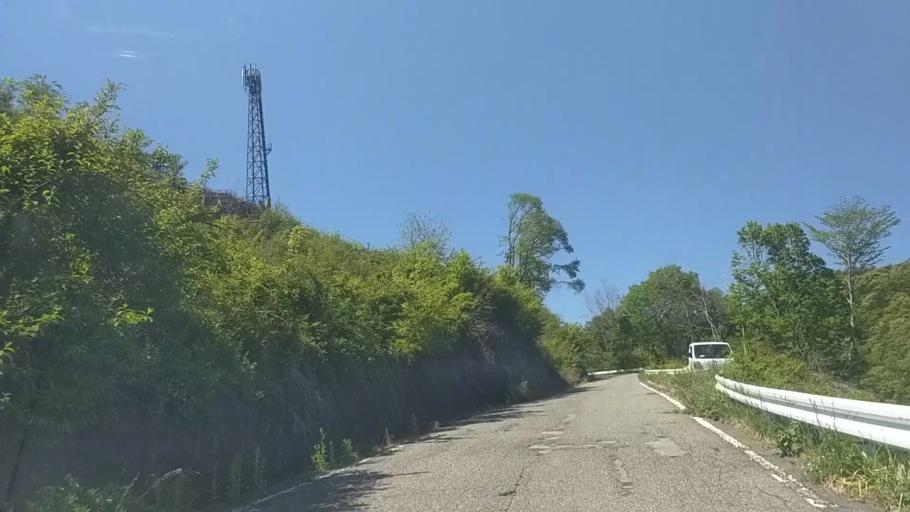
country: JP
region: Yamanashi
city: Nirasaki
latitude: 35.8963
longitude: 138.4505
